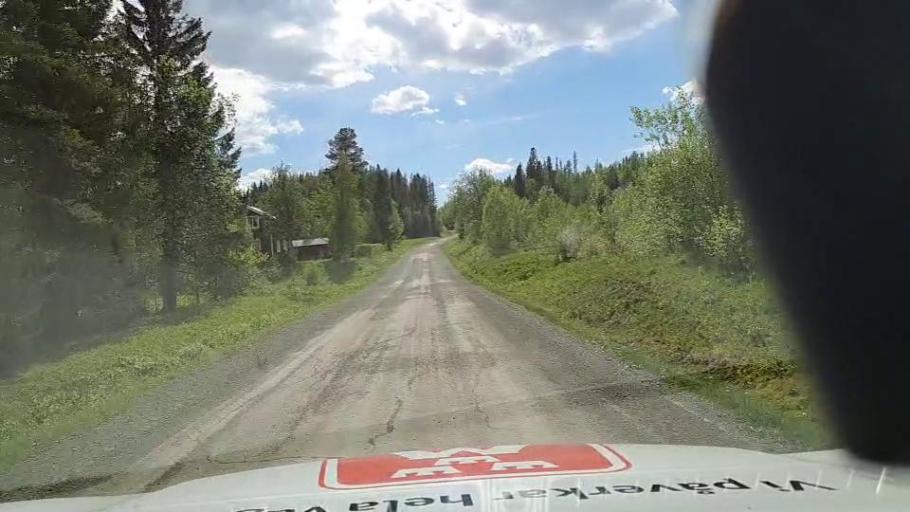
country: SE
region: Vaesterbotten
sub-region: Vilhelmina Kommun
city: Sjoberg
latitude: 64.5656
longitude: 15.8515
